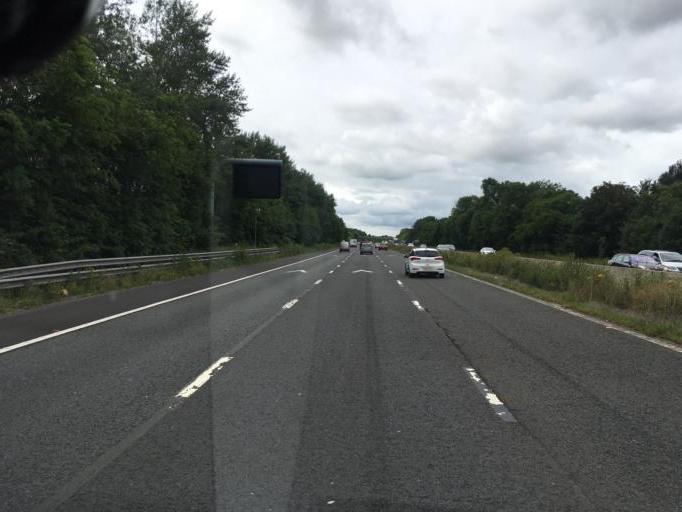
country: GB
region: England
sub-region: Gloucestershire
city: Painswick
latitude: 51.8149
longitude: -2.2343
